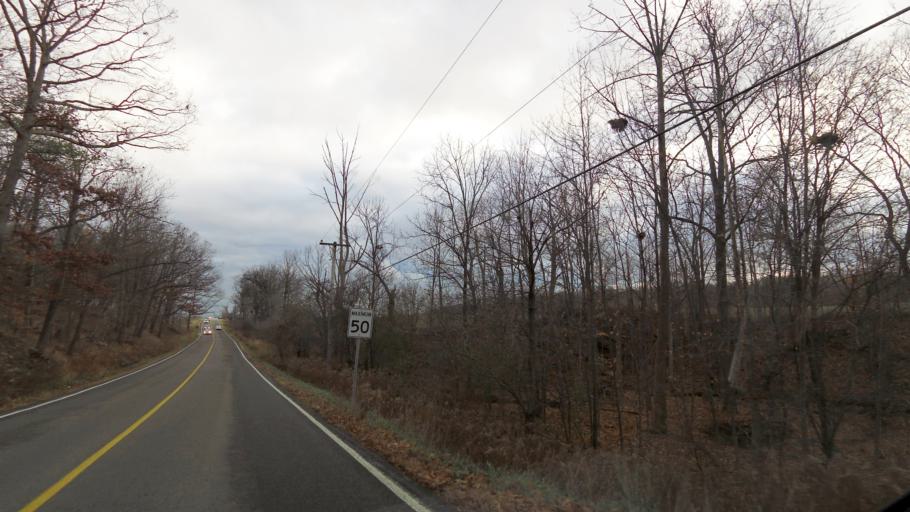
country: CA
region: Ontario
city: Burlington
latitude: 43.4032
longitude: -79.8388
